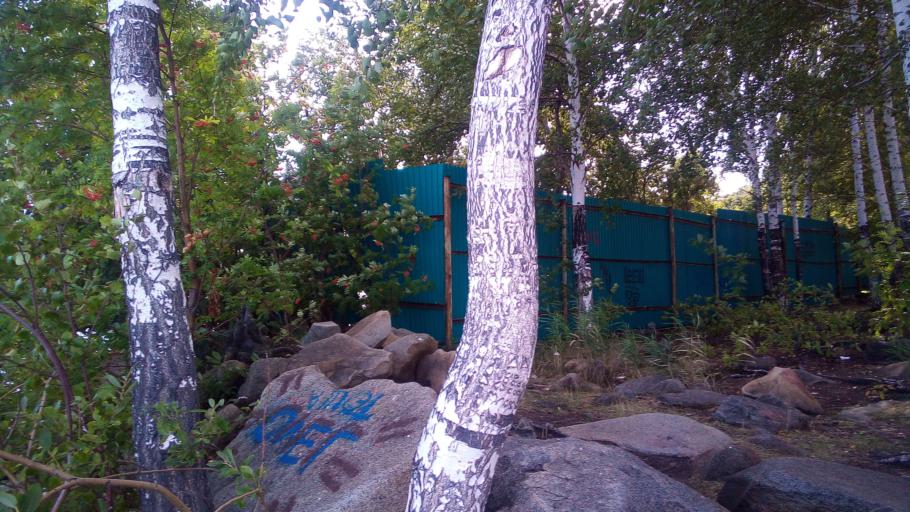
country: RU
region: Chelyabinsk
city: Tayginka
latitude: 55.4807
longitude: 60.4977
